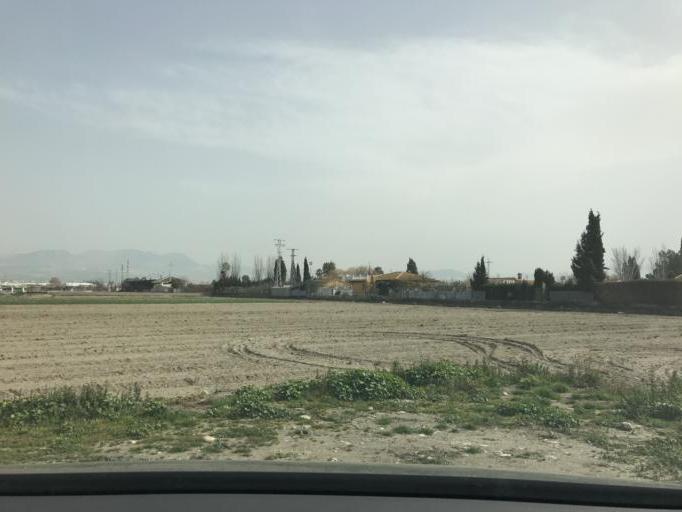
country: ES
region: Andalusia
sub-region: Provincia de Granada
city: Atarfe
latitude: 37.1960
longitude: -3.6782
